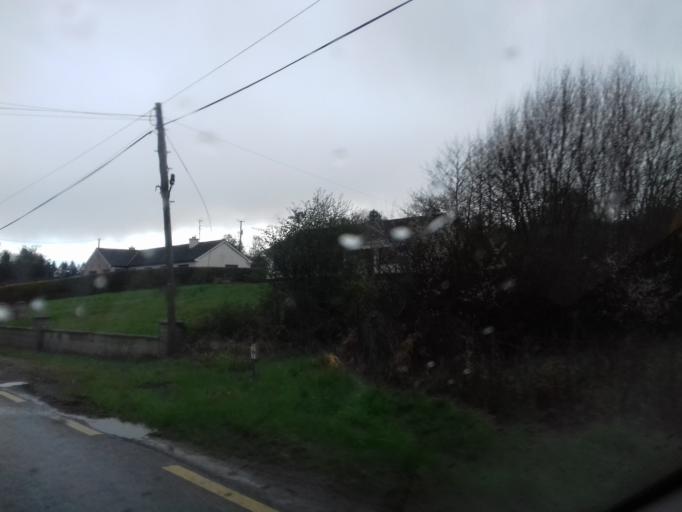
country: IE
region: Connaught
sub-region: County Leitrim
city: Manorhamilton
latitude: 54.2753
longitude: -7.9372
